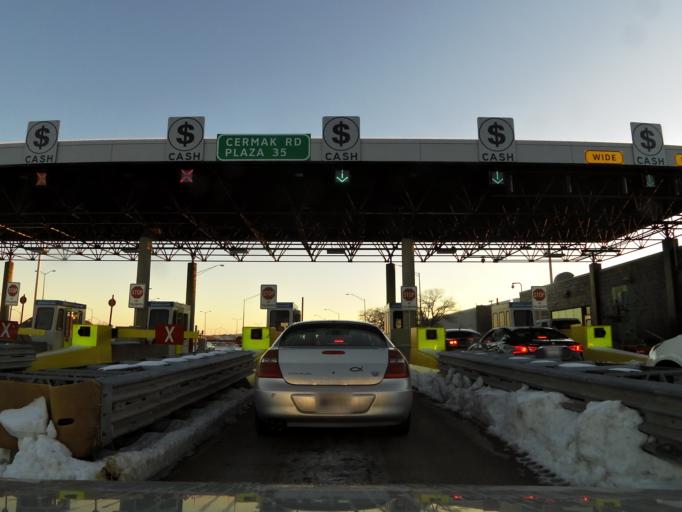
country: US
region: Illinois
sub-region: DuPage County
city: Oak Brook
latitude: 41.8533
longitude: -87.9200
